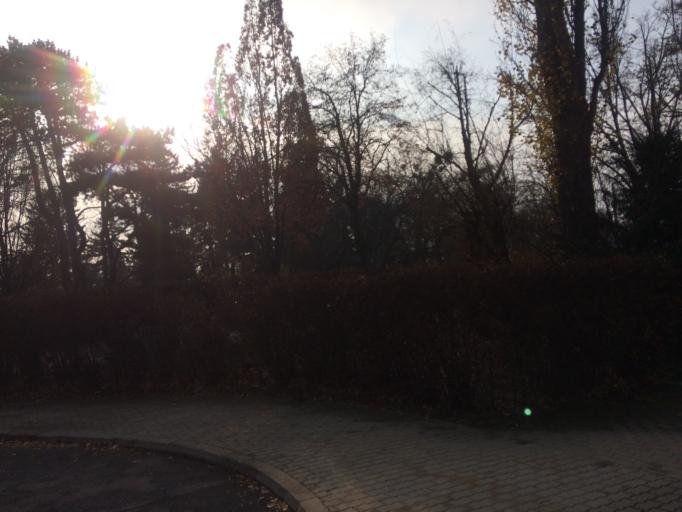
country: AT
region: Vienna
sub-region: Wien Stadt
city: Vienna
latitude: 48.2372
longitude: 16.3336
